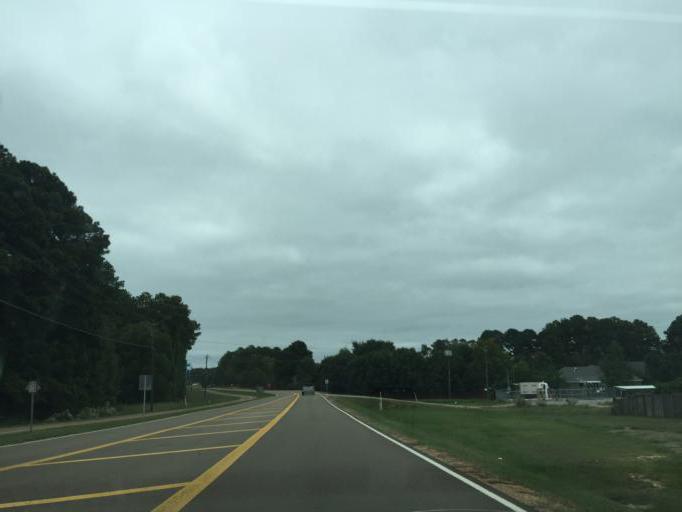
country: US
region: Mississippi
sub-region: Madison County
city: Madison
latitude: 32.4062
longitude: -90.0083
